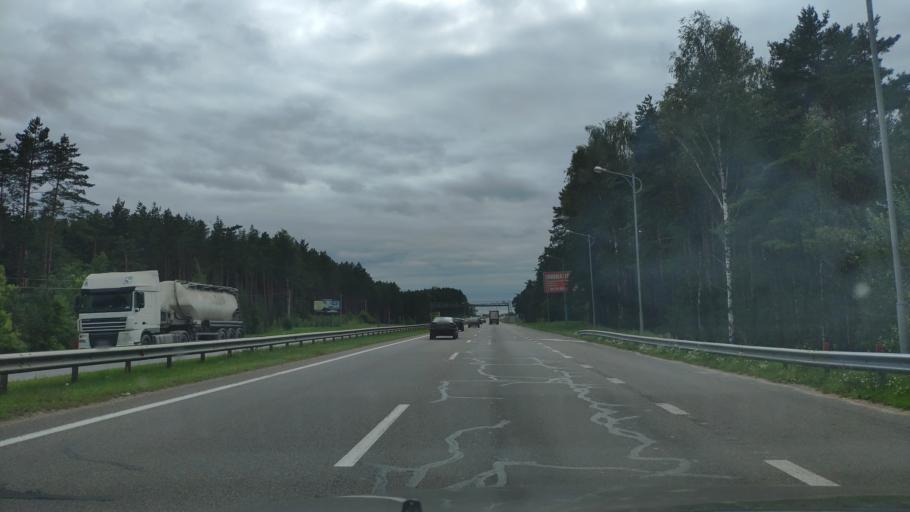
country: BY
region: Minsk
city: Zhdanovichy
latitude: 53.9472
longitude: 27.3677
